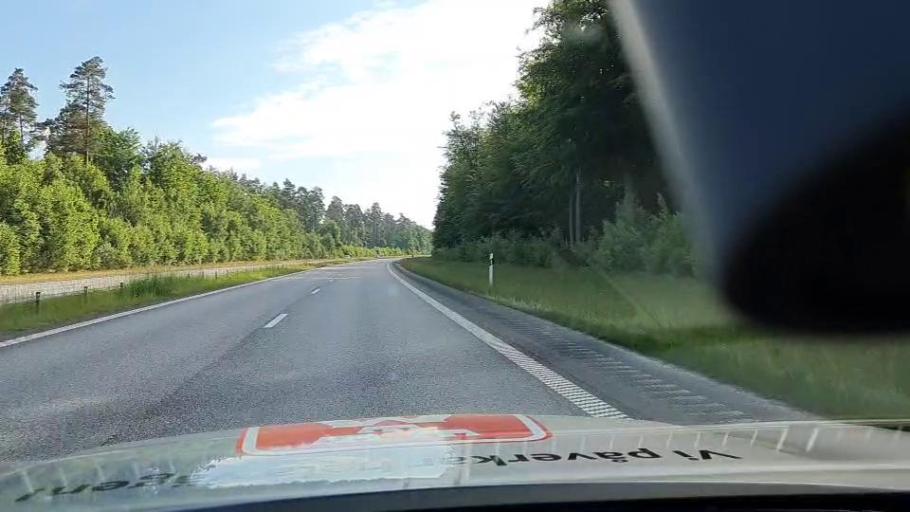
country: SE
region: Skane
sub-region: Bromolla Kommun
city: Bromoella
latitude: 56.0576
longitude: 14.4510
